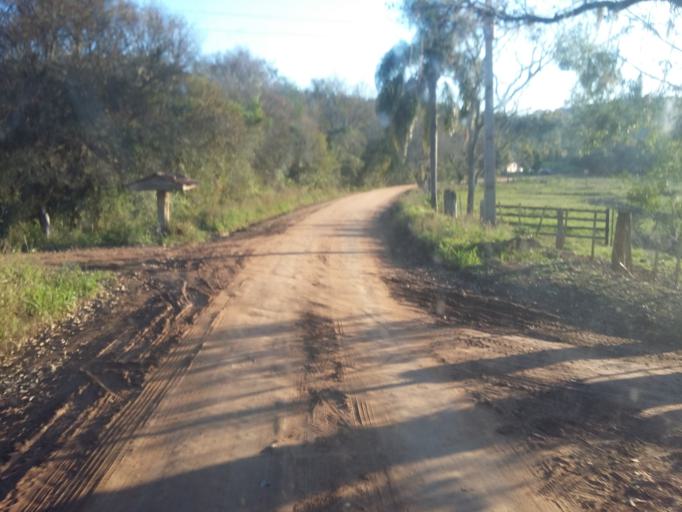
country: BR
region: Rio Grande do Sul
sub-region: Camaqua
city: Camaqua
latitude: -30.7253
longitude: -51.7731
